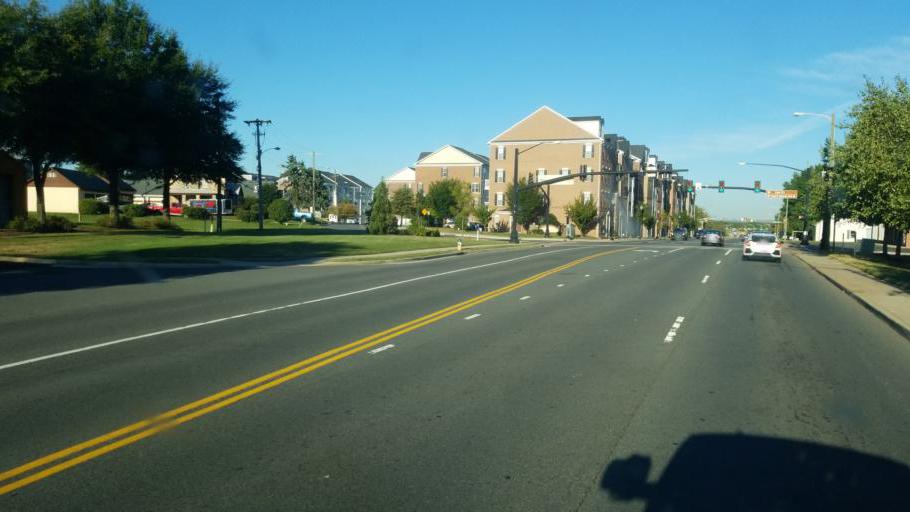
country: US
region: Virginia
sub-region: City of Manassas
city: Manassas
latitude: 38.7514
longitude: -77.4816
